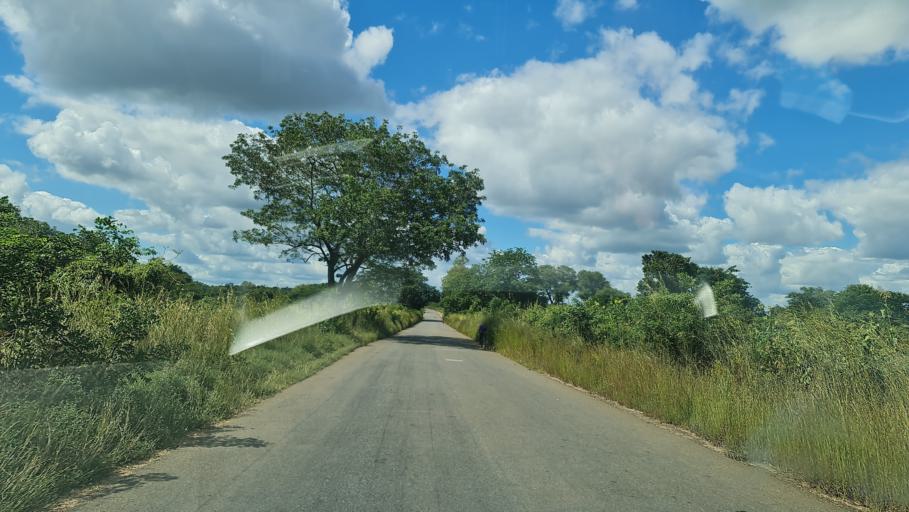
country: MZ
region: Zambezia
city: Quelimane
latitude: -17.5098
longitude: 36.2311
